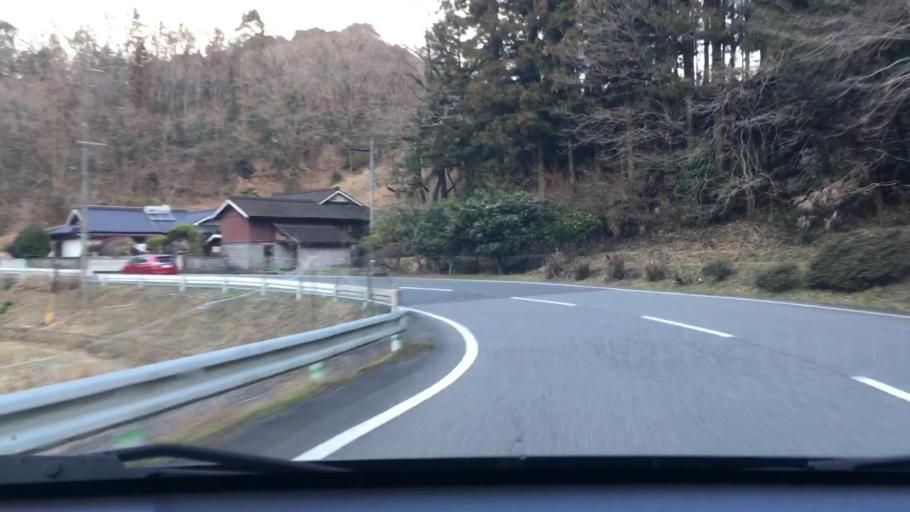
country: JP
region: Oita
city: Bungo-Takada-shi
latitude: 33.4612
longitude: 131.3894
